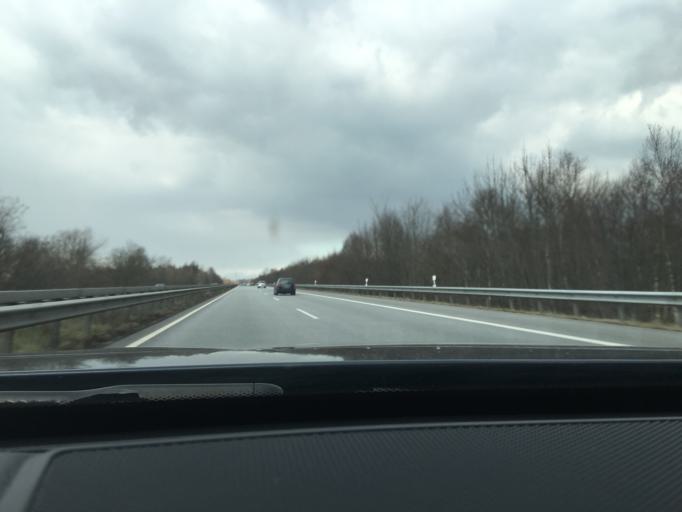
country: DE
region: Lower Saxony
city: Driftsethe
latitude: 53.4161
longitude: 8.5806
